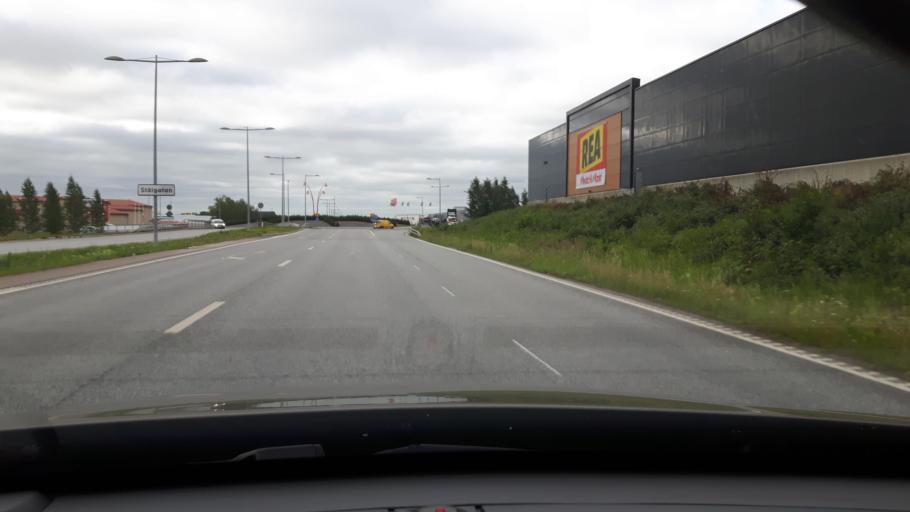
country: SE
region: Uppsala
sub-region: Uppsala Kommun
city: Saevja
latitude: 59.8561
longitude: 17.6825
